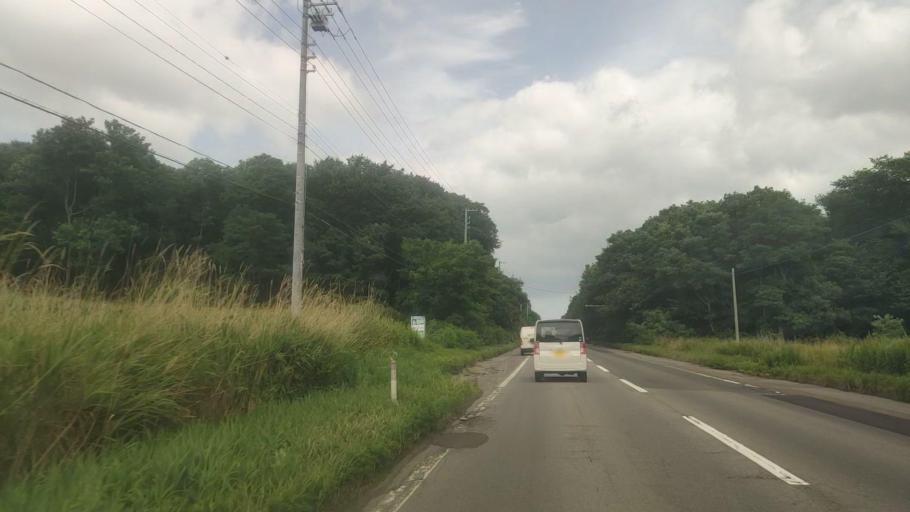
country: JP
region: Hokkaido
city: Nanae
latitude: 42.0453
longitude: 140.6027
